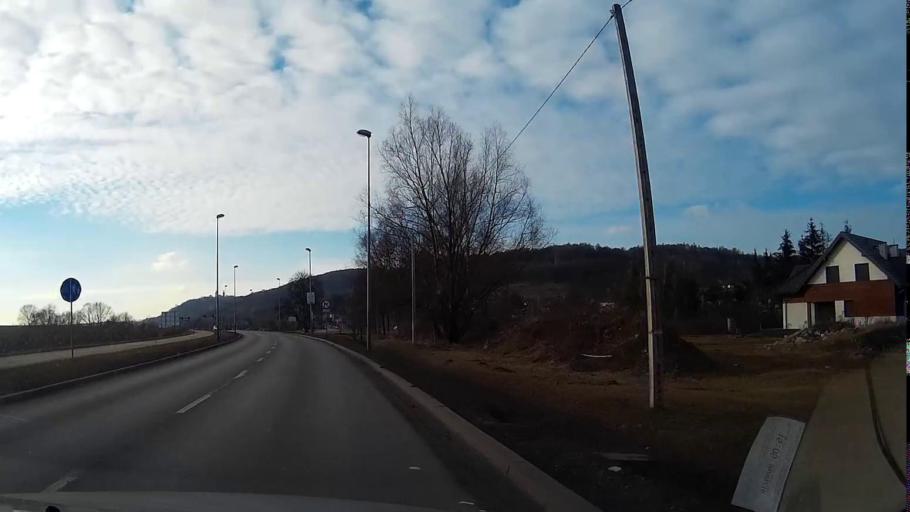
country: PL
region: Lesser Poland Voivodeship
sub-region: Krakow
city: Sidzina
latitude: 50.0463
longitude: 19.8759
